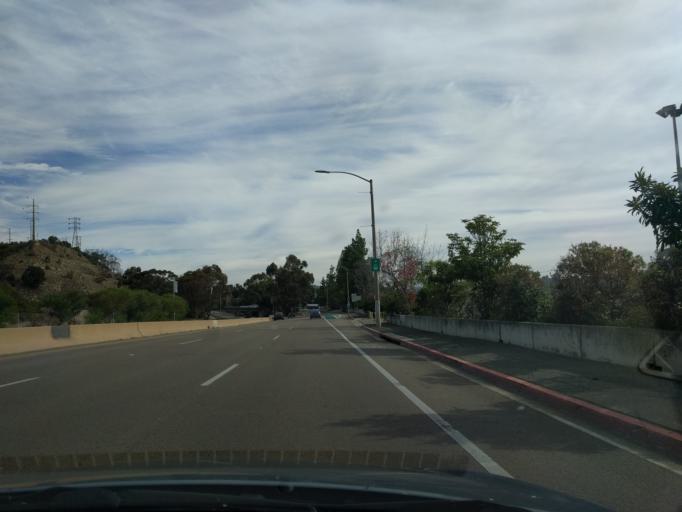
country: US
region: California
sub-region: San Diego County
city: San Diego
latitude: 32.7861
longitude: -117.1233
